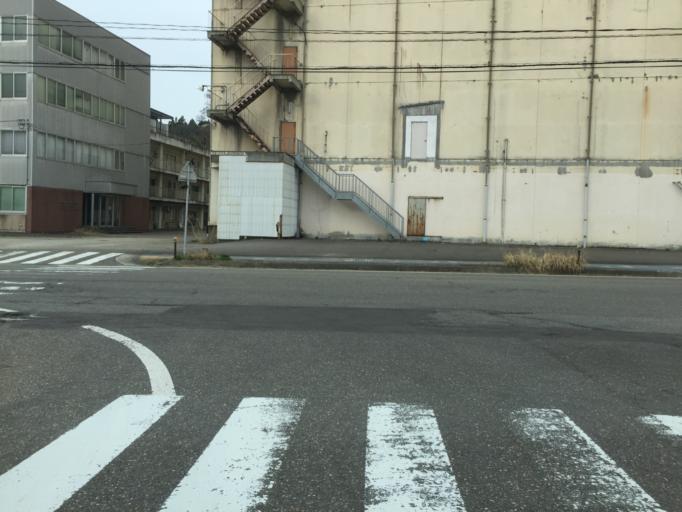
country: JP
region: Niigata
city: Tochio-honcho
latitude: 37.4751
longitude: 138.9999
